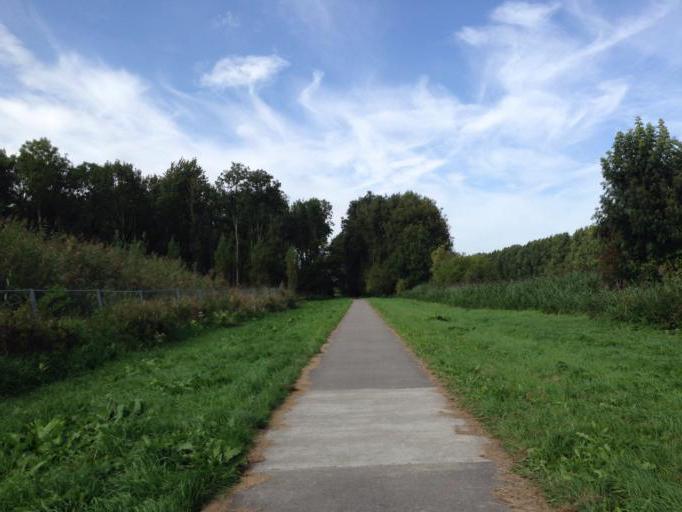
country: NL
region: North Holland
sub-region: Gemeente Huizen
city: Huizen
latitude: 52.3472
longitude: 5.2809
